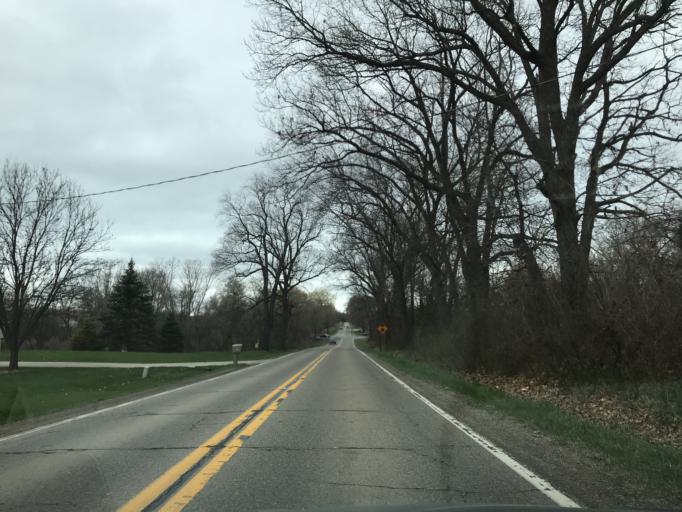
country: US
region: Michigan
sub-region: Oakland County
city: South Lyon
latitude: 42.4970
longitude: -83.6859
